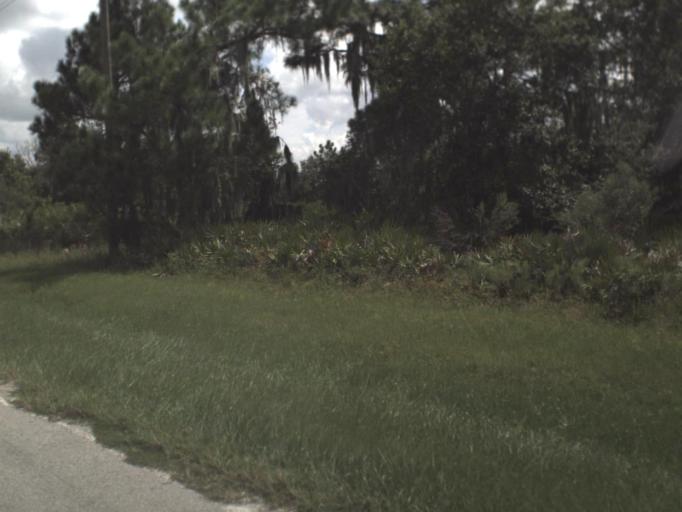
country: US
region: Florida
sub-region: Hillsborough County
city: Wimauma
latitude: 27.4635
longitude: -82.1875
